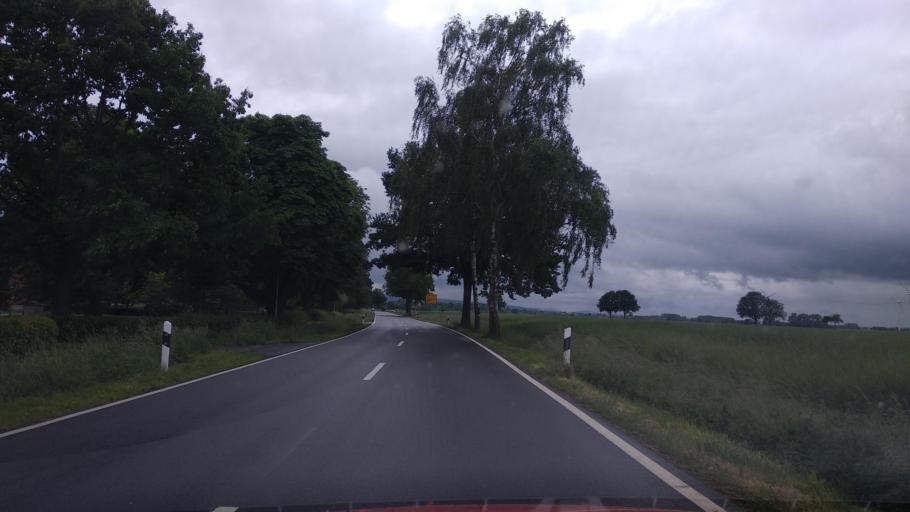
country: DE
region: Lower Saxony
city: Ludersfeld
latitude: 52.3545
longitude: 9.2439
